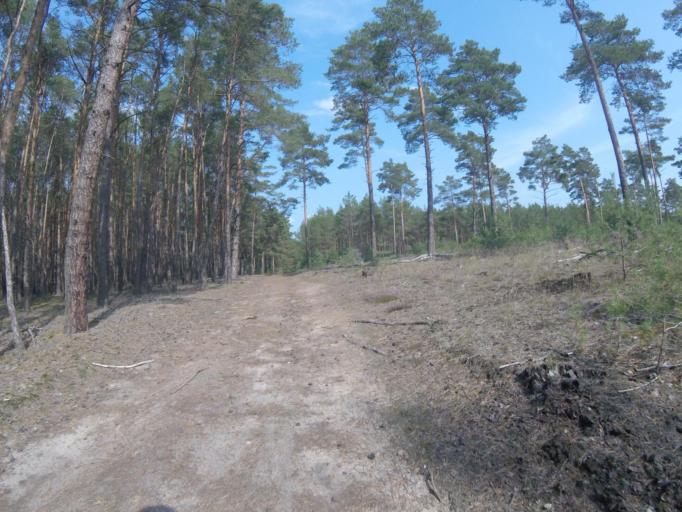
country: DE
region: Brandenburg
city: Bestensee
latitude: 52.2749
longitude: 13.7046
